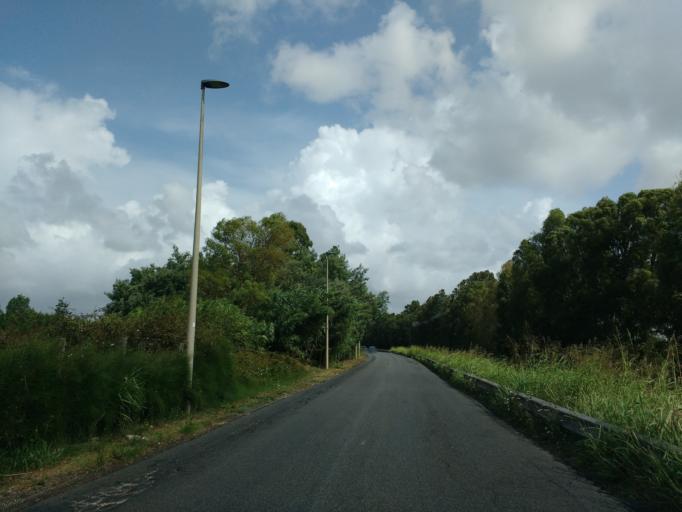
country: IT
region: Latium
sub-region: Citta metropolitana di Roma Capitale
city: Acilia-Castel Fusano-Ostia Antica
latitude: 41.7579
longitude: 12.3298
